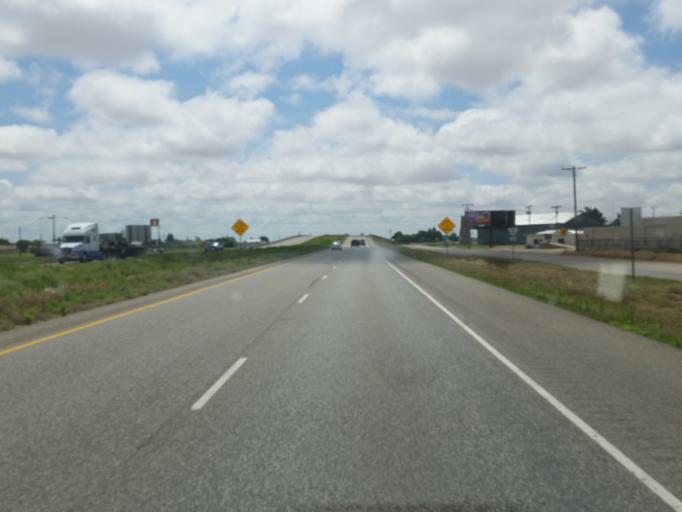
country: US
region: Texas
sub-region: Lubbock County
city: Slaton
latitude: 33.4223
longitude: -101.6470
